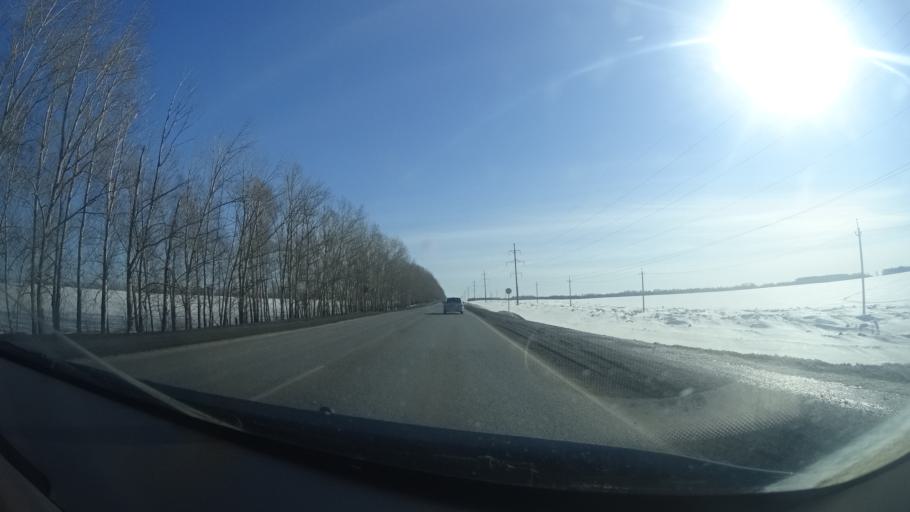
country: RU
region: Bashkortostan
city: Mikhaylovka
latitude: 54.8549
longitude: 55.7657
